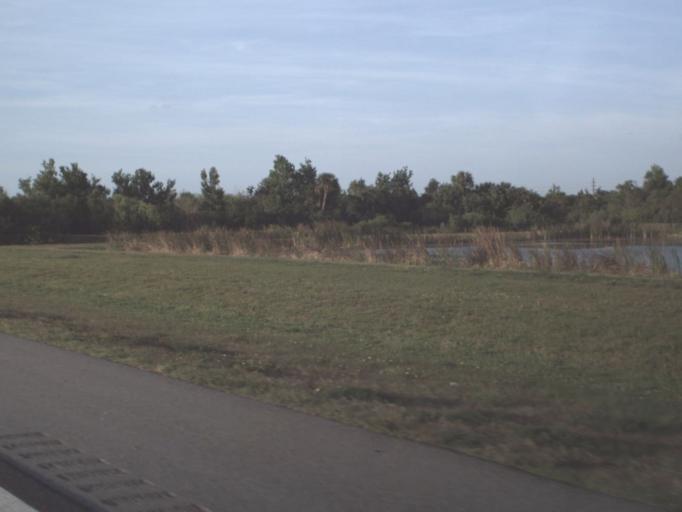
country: US
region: Florida
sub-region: Brevard County
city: Titusville
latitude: 28.5641
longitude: -80.8514
